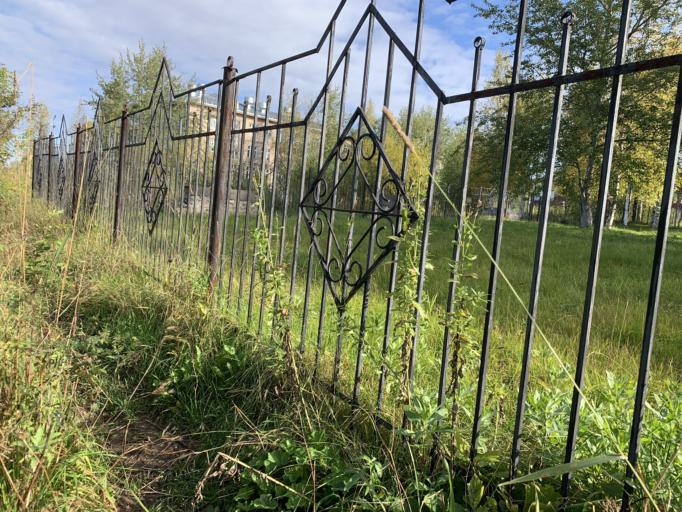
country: RU
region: Perm
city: Gubakha
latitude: 58.8374
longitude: 57.5587
